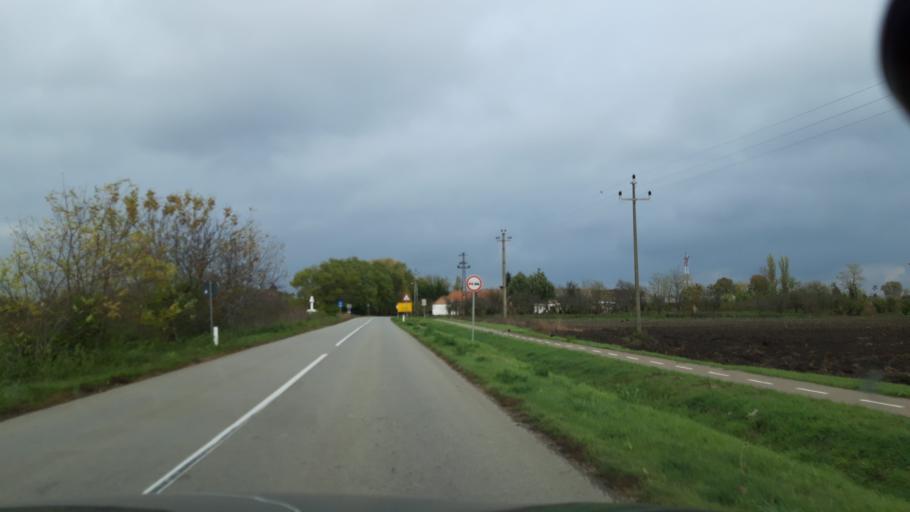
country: HU
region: Csongrad
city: Roszke
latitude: 46.1493
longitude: 20.1030
